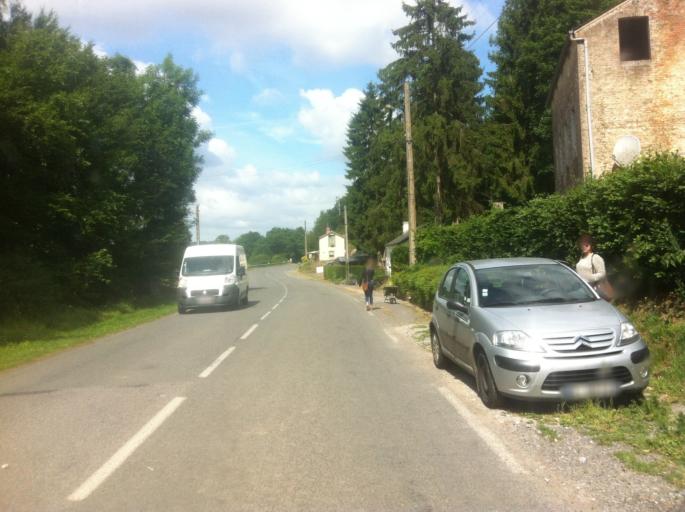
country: BE
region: Wallonia
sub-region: Province du Hainaut
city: Momignies
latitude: 50.1207
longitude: 4.1727
